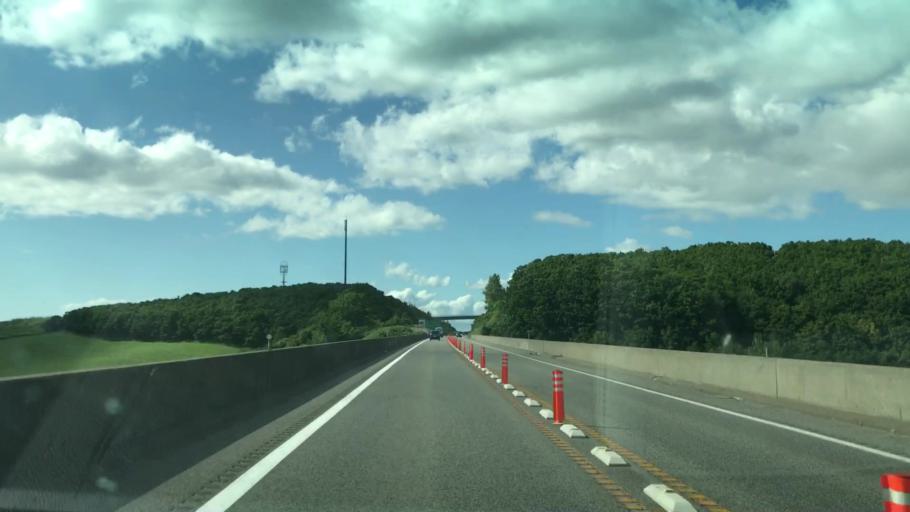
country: JP
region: Hokkaido
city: Muroran
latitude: 42.3934
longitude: 140.9567
